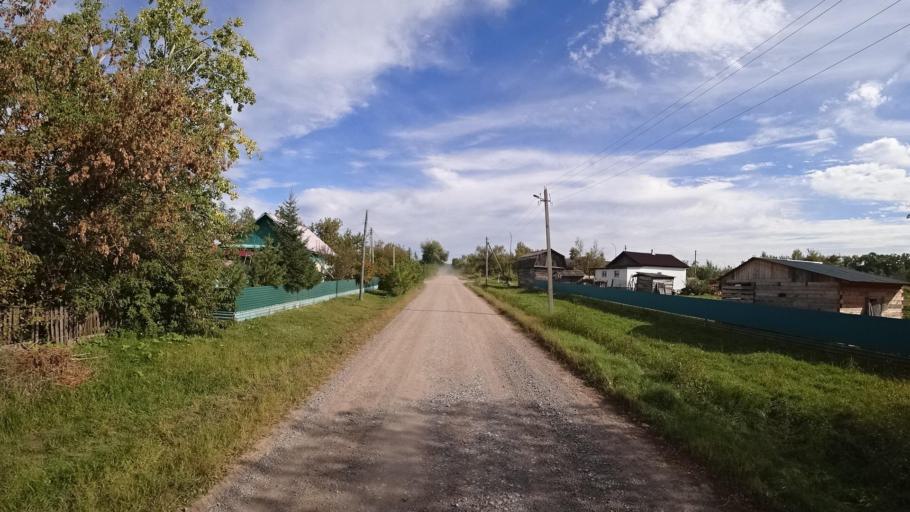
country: RU
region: Primorskiy
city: Dostoyevka
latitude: 44.3043
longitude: 133.4550
